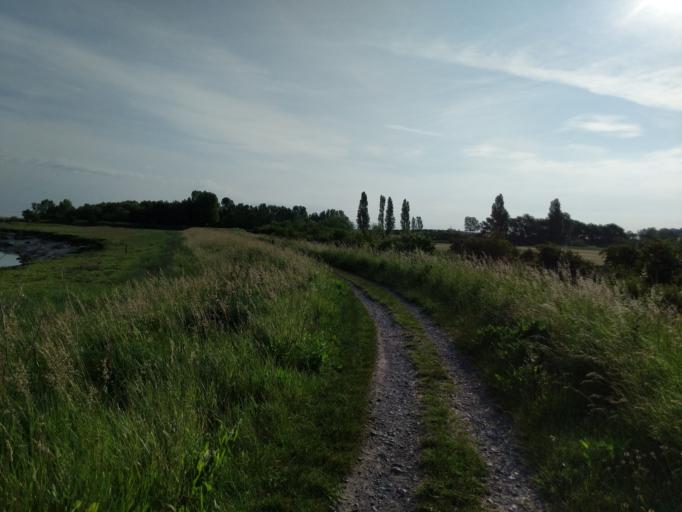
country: GB
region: England
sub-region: Kent
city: Faversham
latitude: 51.3263
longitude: 0.9153
